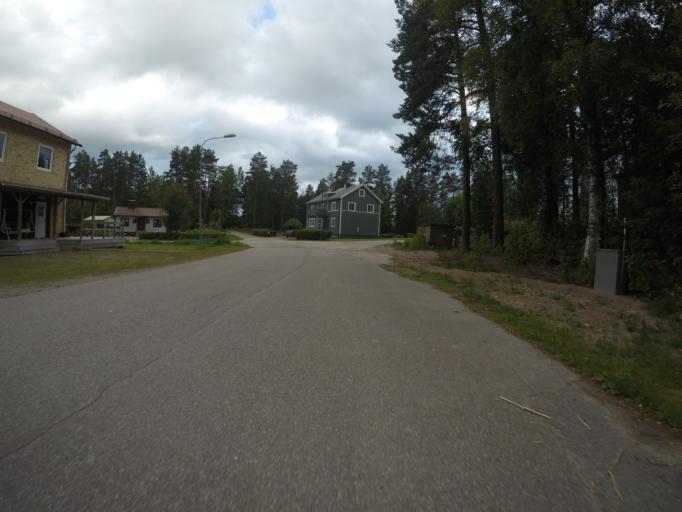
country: SE
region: Vaermland
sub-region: Filipstads Kommun
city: Lesjofors
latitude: 60.1410
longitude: 14.3868
